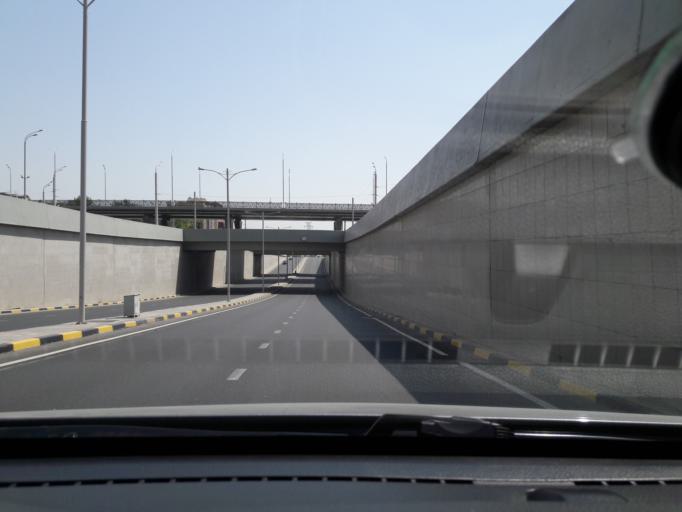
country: TJ
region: Dushanbe
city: Dushanbe
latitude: 38.5844
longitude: 68.7410
